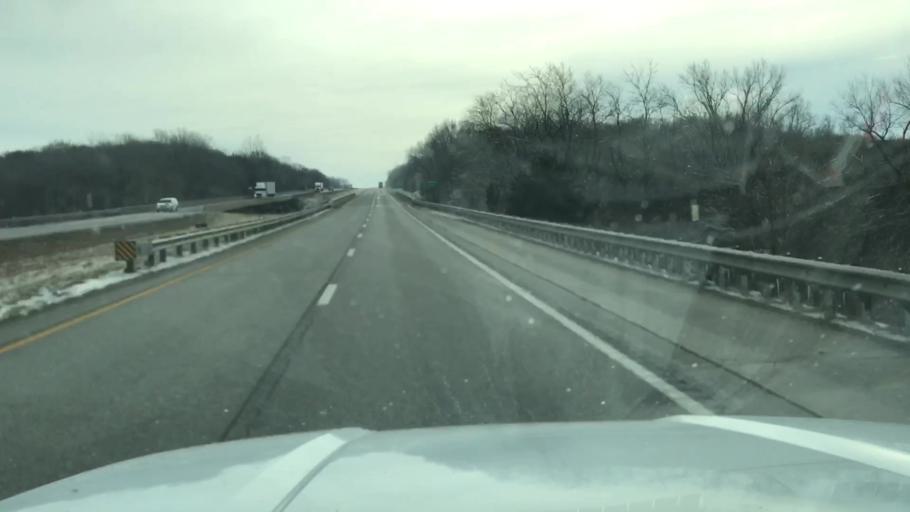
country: US
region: Missouri
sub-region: Andrew County
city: Savannah
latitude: 39.9024
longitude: -94.8829
